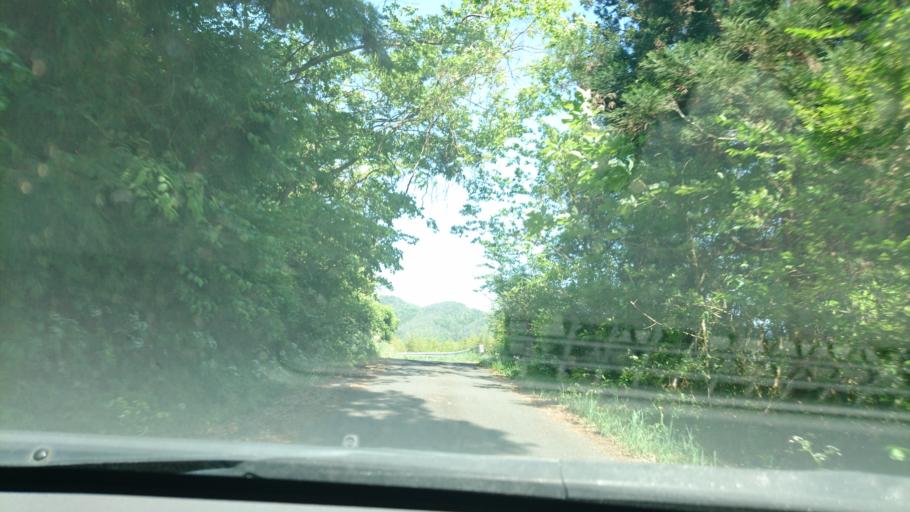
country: JP
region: Iwate
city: Ichinoseki
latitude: 38.9385
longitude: 141.2412
